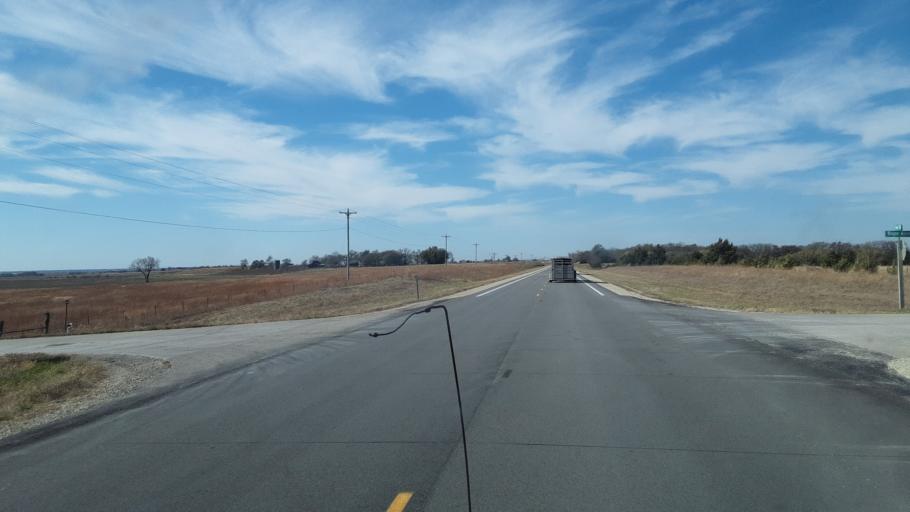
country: US
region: Kansas
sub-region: Marion County
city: Marion
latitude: 38.3629
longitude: -96.9478
